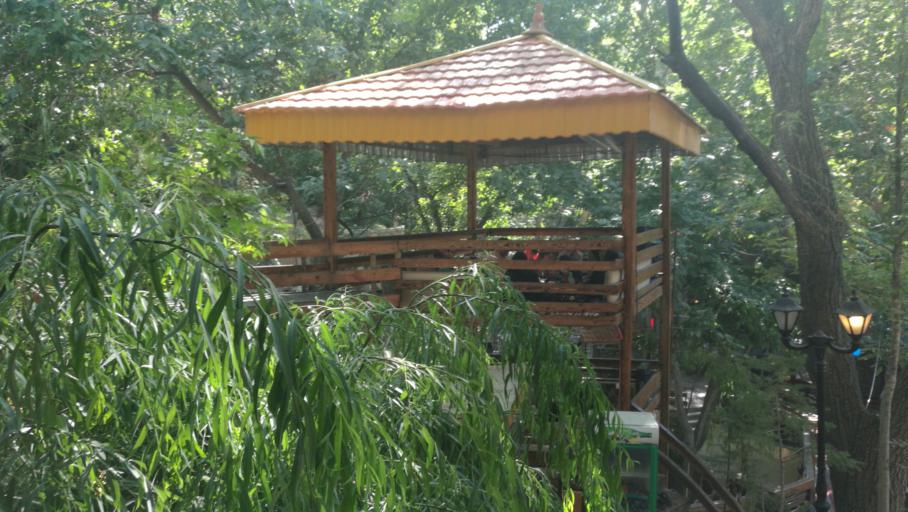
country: IR
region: Razavi Khorasan
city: Torqabeh
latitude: 36.3781
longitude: 59.2617
